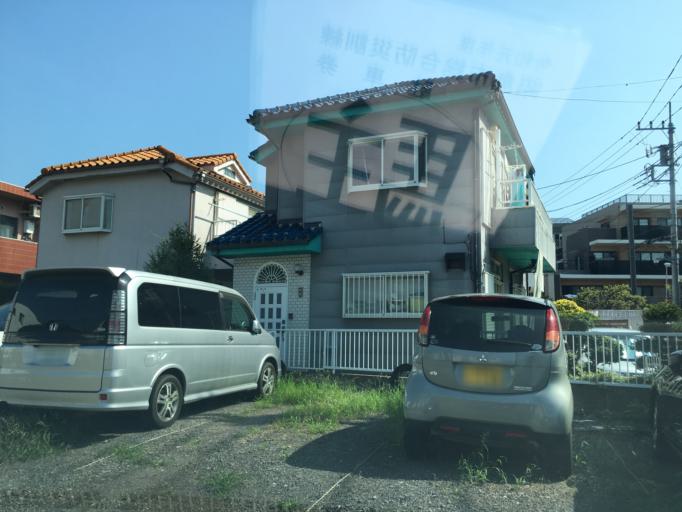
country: JP
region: Tokyo
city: Fussa
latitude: 35.7174
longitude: 139.3446
